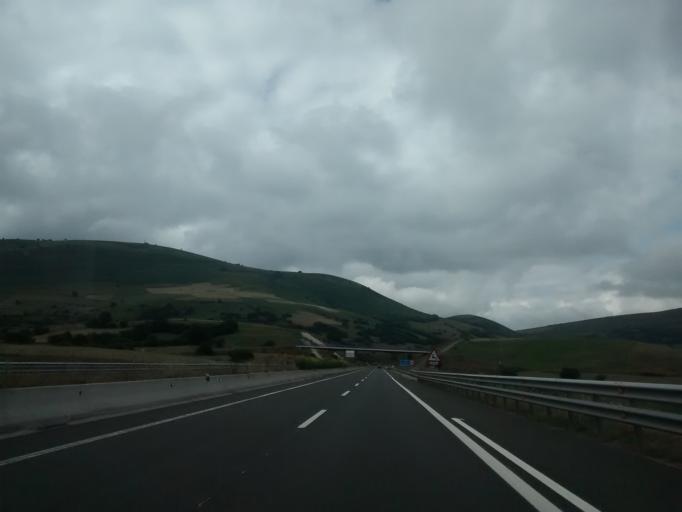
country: ES
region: Cantabria
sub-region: Provincia de Cantabria
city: Pesquera
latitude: 43.0740
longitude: -4.0857
